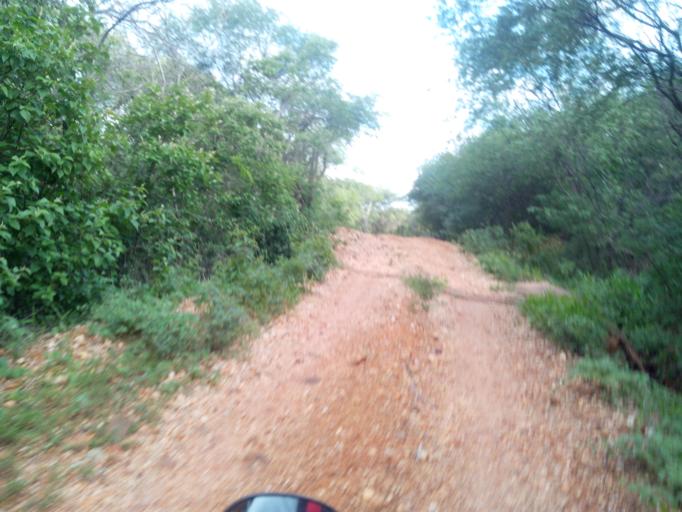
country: BR
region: Piaui
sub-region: Sao Raimundo Nonato
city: Sao Raimundo Nonato
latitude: -8.7844
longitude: -42.4897
